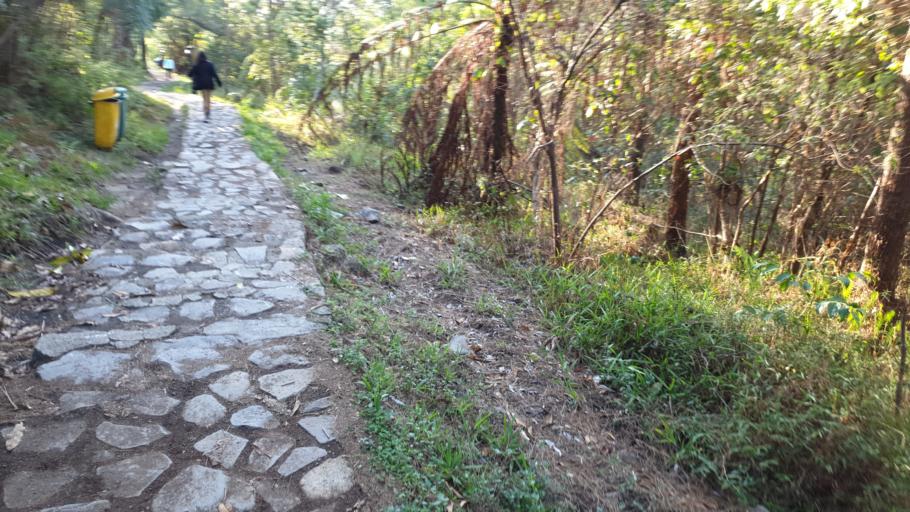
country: ID
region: East Nusa Tenggara
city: Koanara
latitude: -8.7714
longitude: 121.8168
